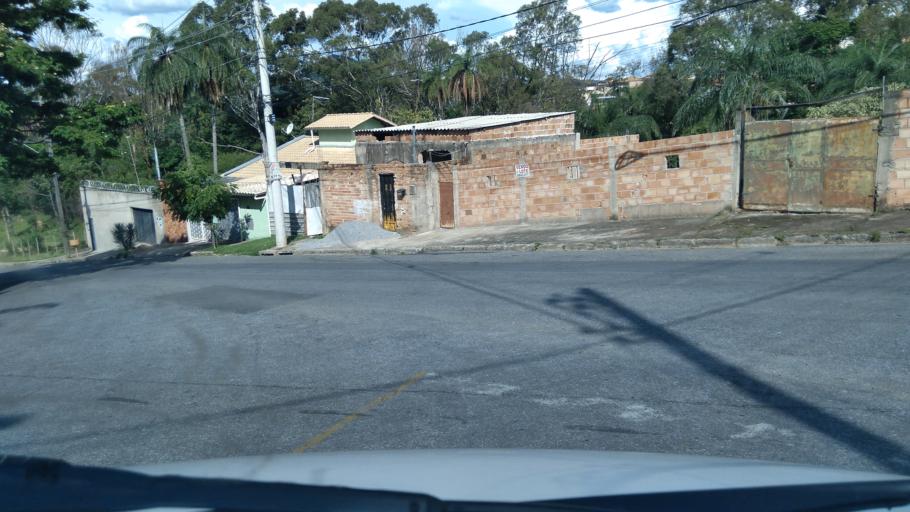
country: BR
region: Minas Gerais
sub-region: Belo Horizonte
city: Belo Horizonte
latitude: -19.8565
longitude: -43.8773
